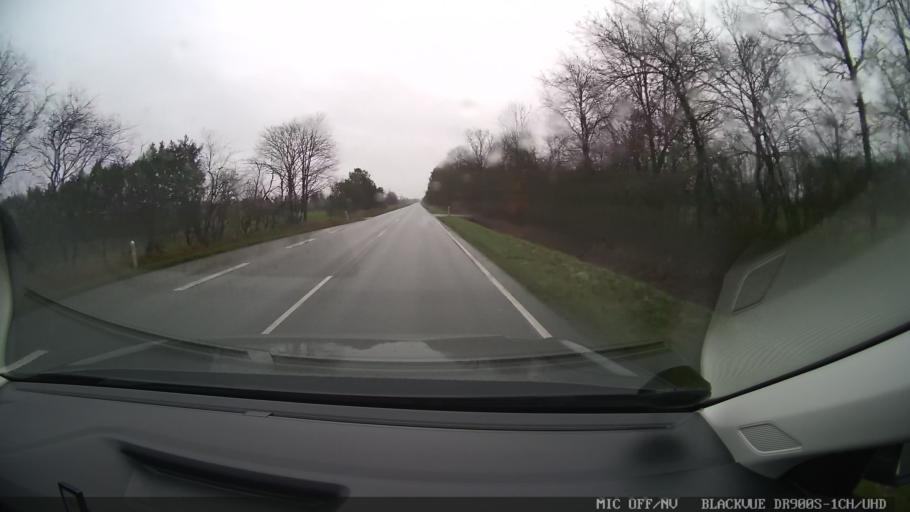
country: DK
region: Central Jutland
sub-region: Herning Kommune
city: Avlum
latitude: 56.2900
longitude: 8.9169
